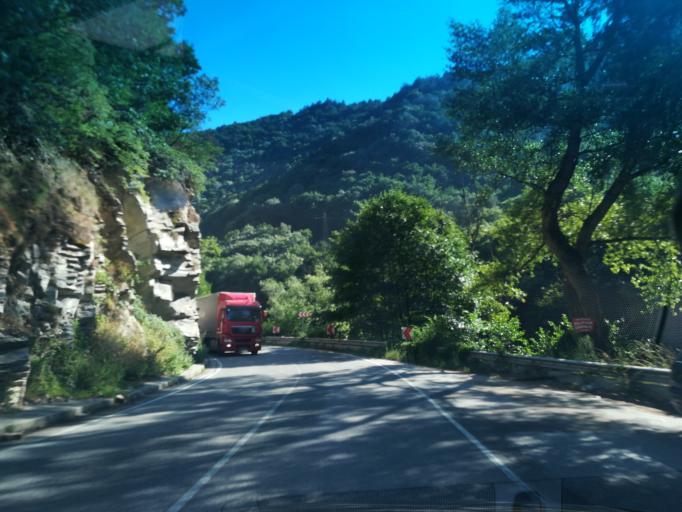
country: BG
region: Plovdiv
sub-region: Obshtina Asenovgrad
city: Asenovgrad
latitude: 41.9391
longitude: 24.8470
